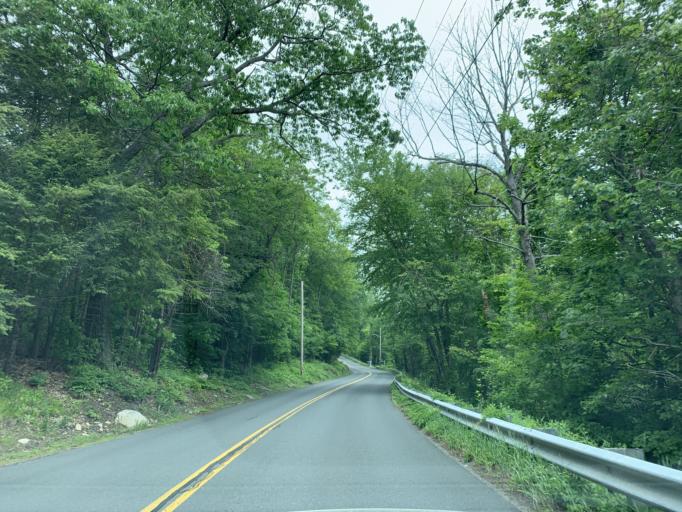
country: US
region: Massachusetts
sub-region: Hampshire County
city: Southampton
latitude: 42.1905
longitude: -72.7834
